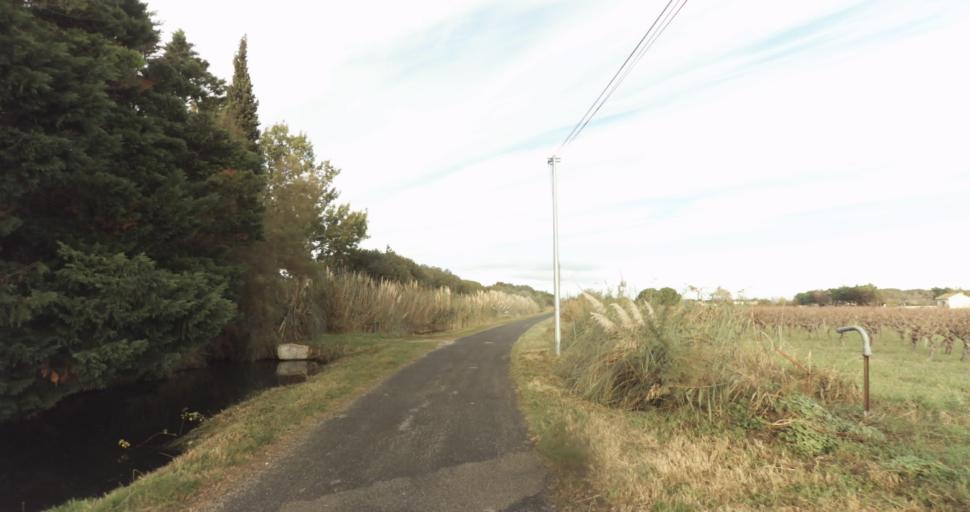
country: FR
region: Languedoc-Roussillon
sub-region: Departement du Gard
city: Aigues-Mortes
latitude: 43.5552
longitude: 4.2087
